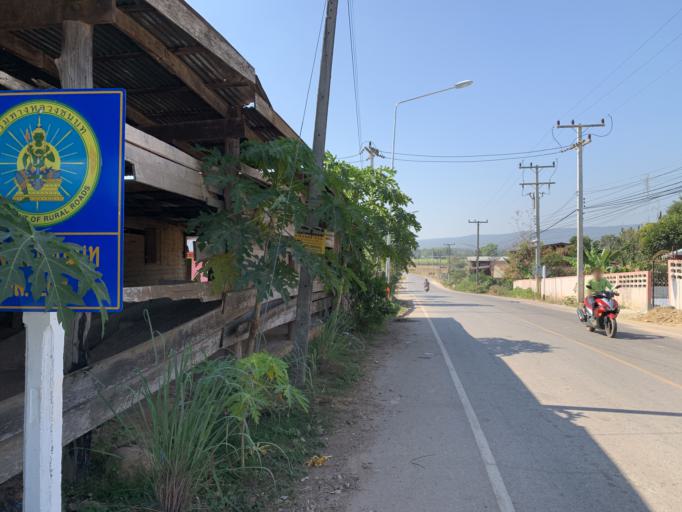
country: TH
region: Phitsanulok
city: Wang Thong
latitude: 16.9688
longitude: 100.5645
